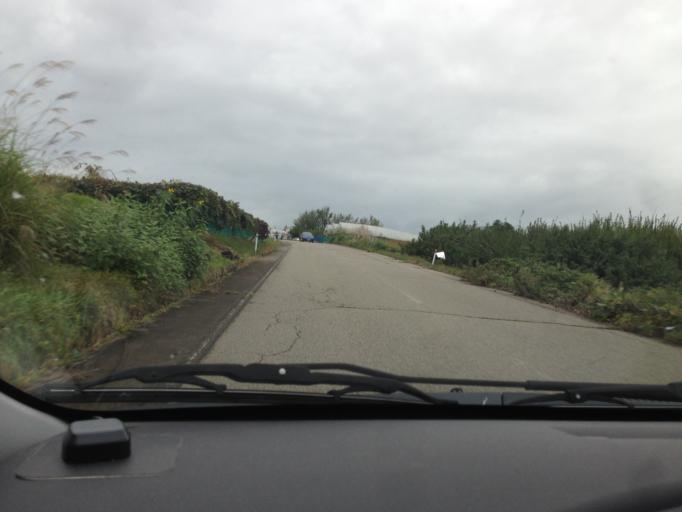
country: JP
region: Fukushima
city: Kitakata
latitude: 37.5017
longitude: 139.8174
